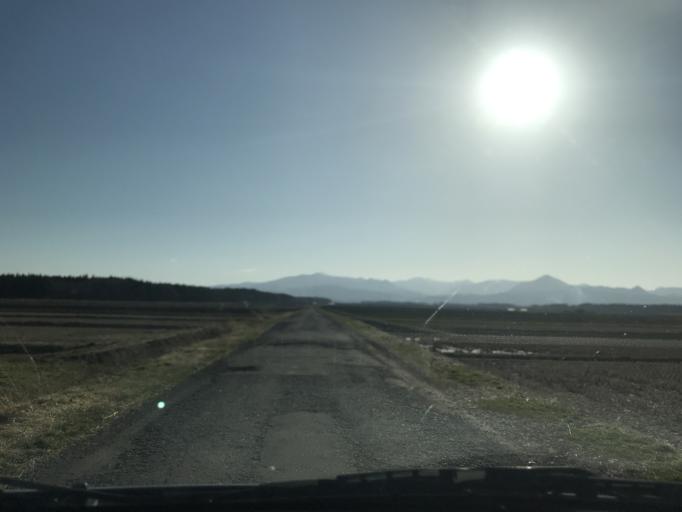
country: JP
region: Iwate
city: Kitakami
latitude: 39.2722
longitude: 141.0652
